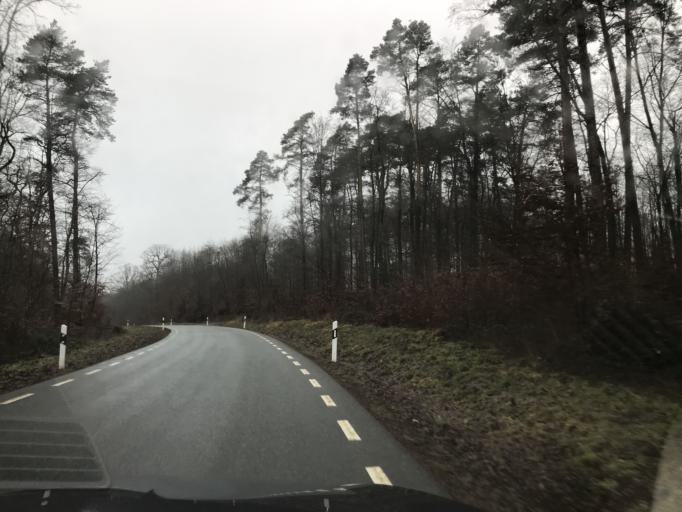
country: DE
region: Baden-Wuerttemberg
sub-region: Regierungsbezirk Stuttgart
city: Weil im Schonbuch
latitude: 48.6120
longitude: 9.0608
